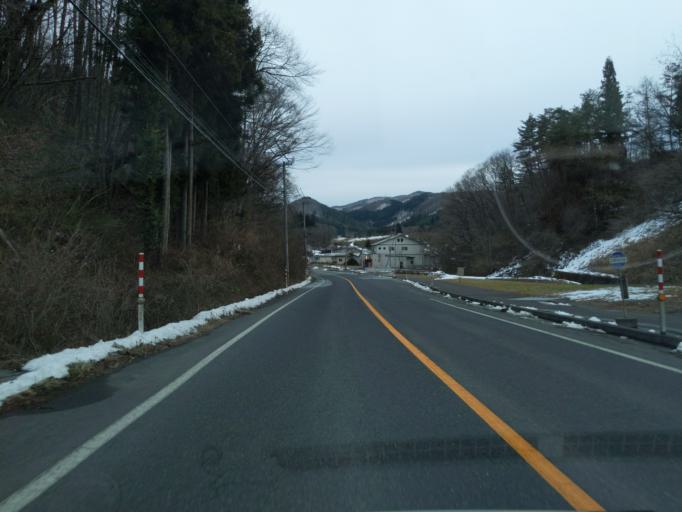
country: JP
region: Iwate
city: Mizusawa
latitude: 39.1222
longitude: 141.2548
